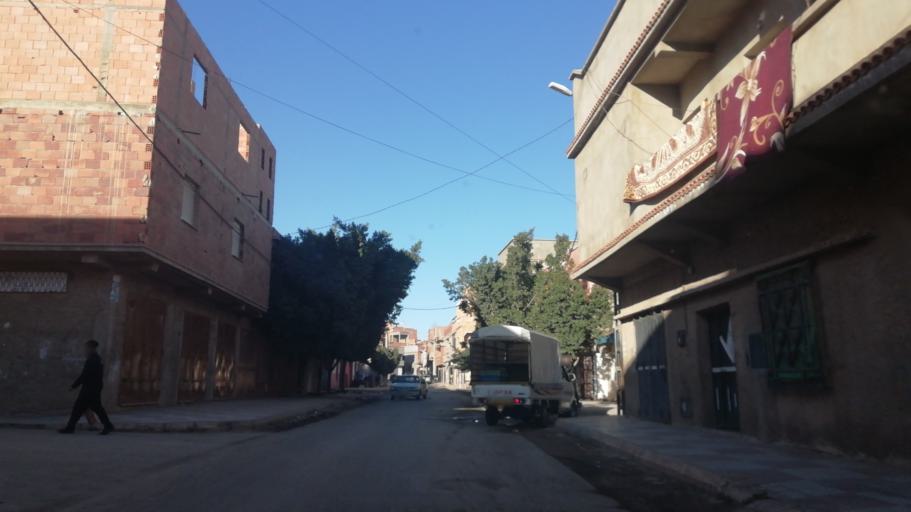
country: DZ
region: Oran
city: Sidi ech Chahmi
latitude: 35.6919
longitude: -0.4947
